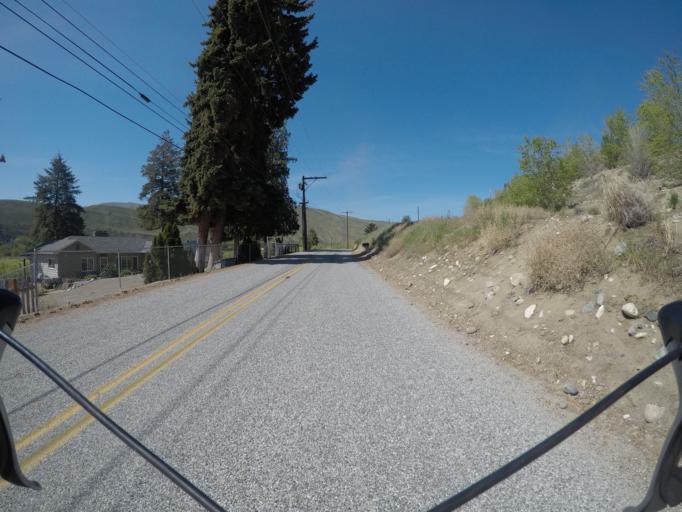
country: US
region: Washington
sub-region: Chelan County
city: Sunnyslope
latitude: 47.4710
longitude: -120.3550
